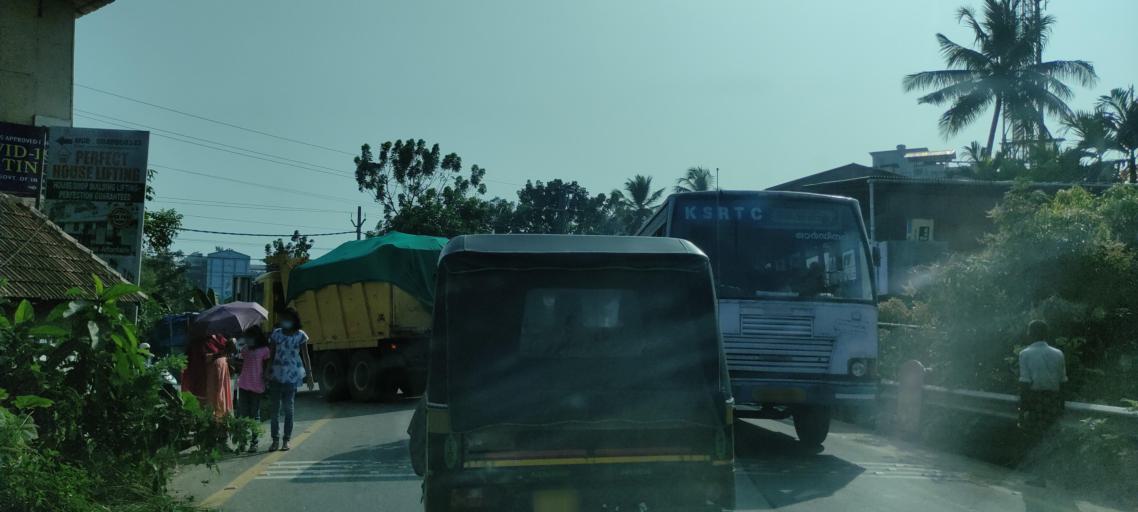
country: IN
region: Kerala
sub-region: Kottayam
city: Changanacheri
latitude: 9.3636
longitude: 76.4763
